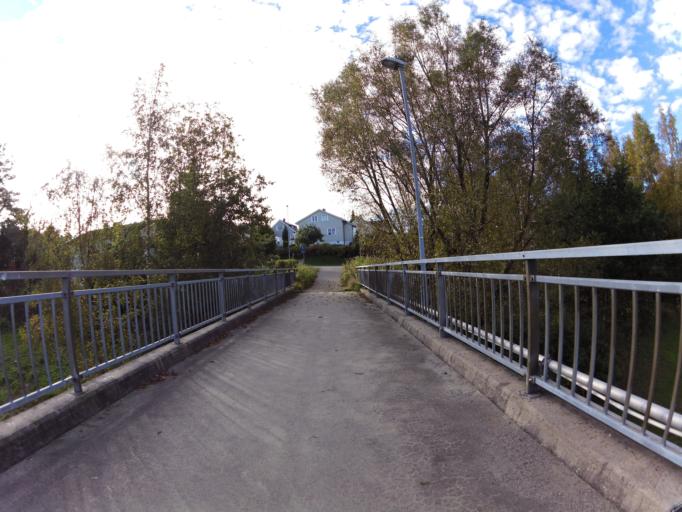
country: NO
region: Ostfold
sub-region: Sarpsborg
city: Sarpsborg
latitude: 59.2817
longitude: 11.0948
